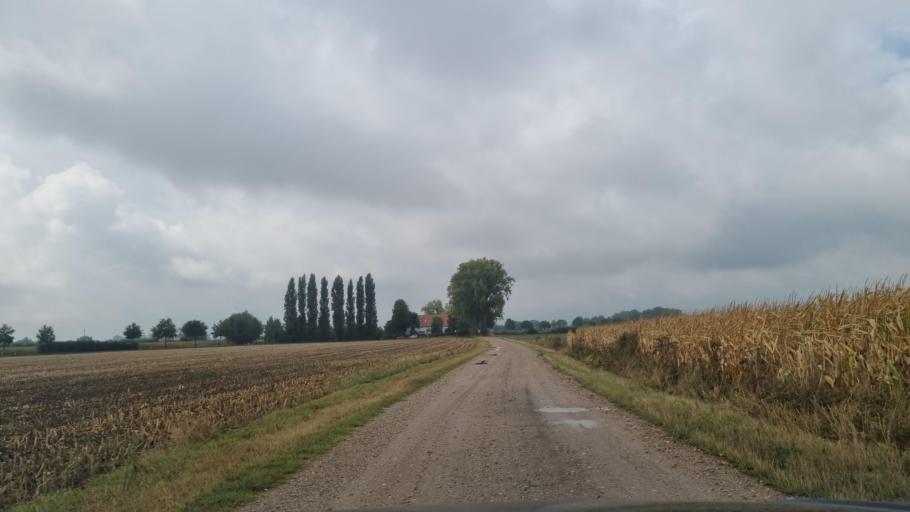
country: DE
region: North Rhine-Westphalia
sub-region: Regierungsbezirk Dusseldorf
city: Kranenburg
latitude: 51.8489
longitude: 6.0465
